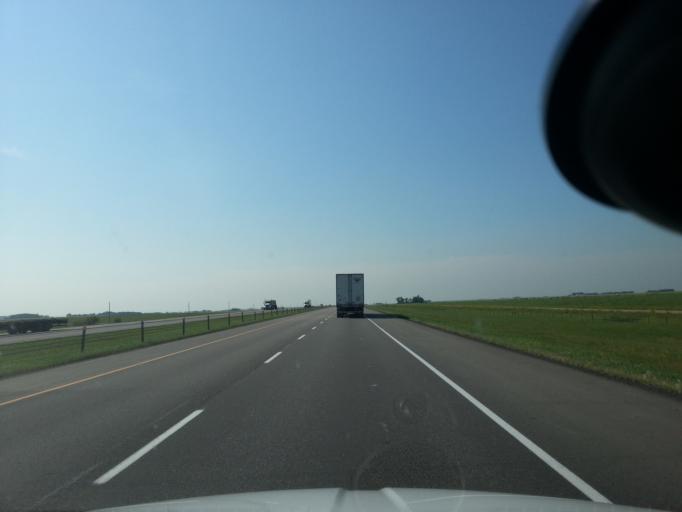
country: CA
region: Alberta
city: Olds
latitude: 51.7217
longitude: -114.0256
